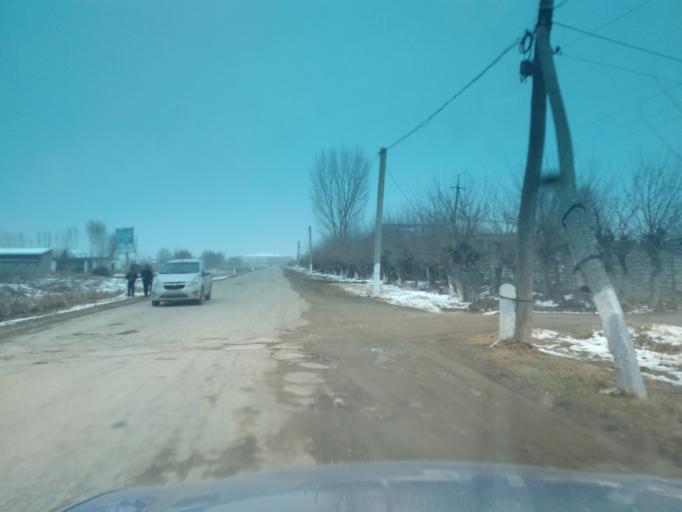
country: UZ
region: Sirdaryo
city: Guliston
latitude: 40.4818
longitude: 68.7514
